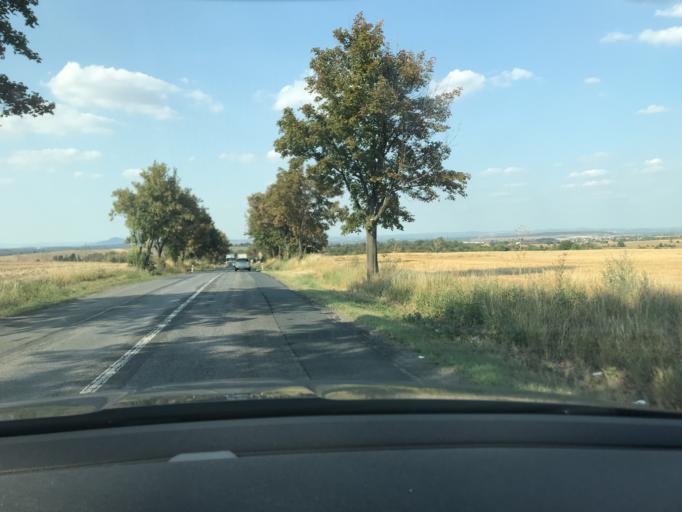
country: CZ
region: Central Bohemia
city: Kralupy nad Vltavou
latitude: 50.2127
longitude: 14.3164
